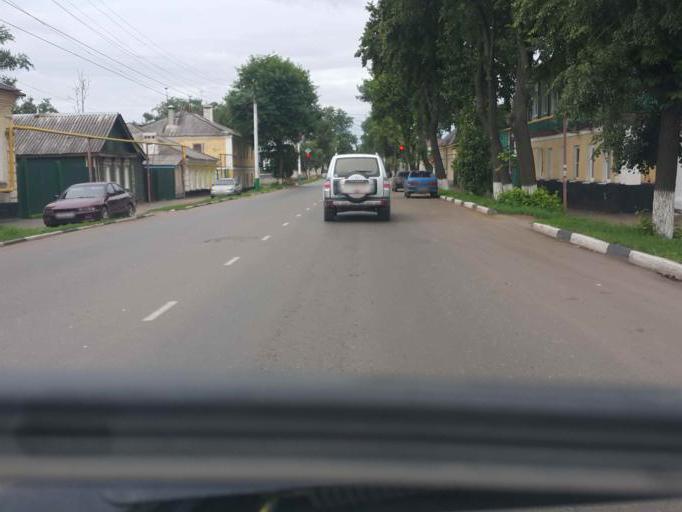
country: RU
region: Tambov
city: Zavoronezhskoye
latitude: 52.8825
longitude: 40.5223
